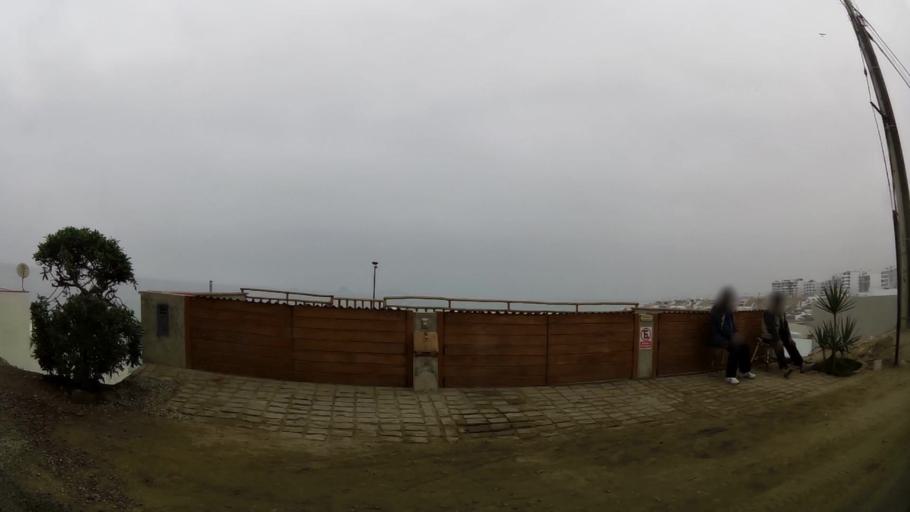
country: PE
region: Lima
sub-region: Lima
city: Punta Hermosa
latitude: -12.3284
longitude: -76.8341
